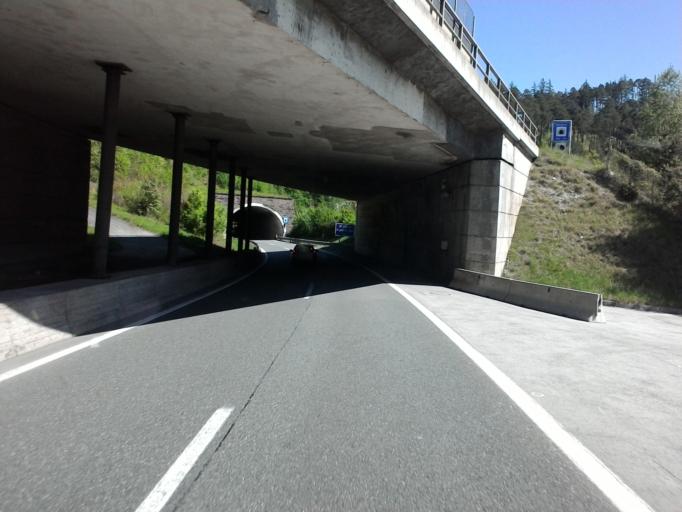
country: AT
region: Tyrol
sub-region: Politischer Bezirk Innsbruck Land
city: Mutters
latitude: 47.2455
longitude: 11.3945
